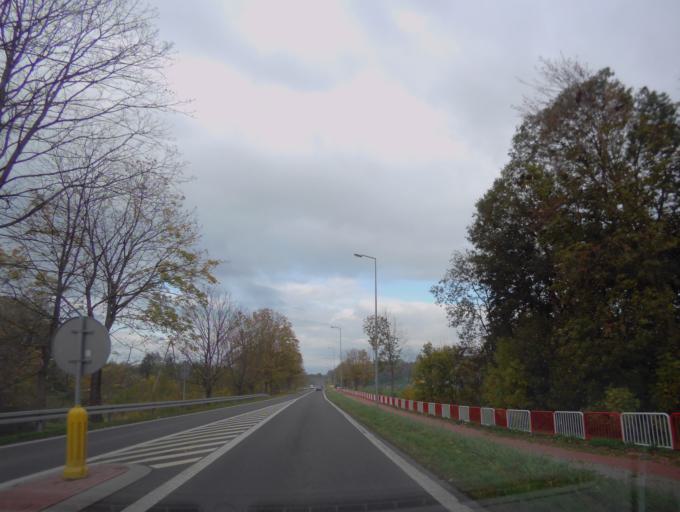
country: PL
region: Lublin Voivodeship
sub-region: Powiat bilgorajski
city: Goraj
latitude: 50.7209
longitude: 22.6725
